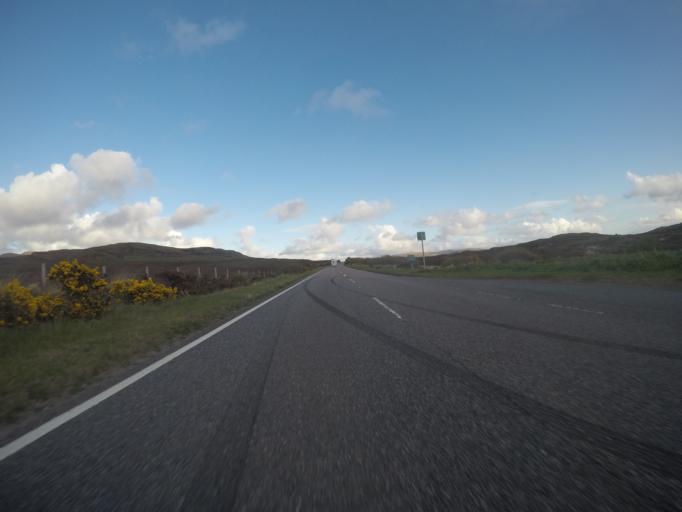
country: GB
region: Scotland
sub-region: Highland
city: Portree
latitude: 57.4720
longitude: -6.2947
